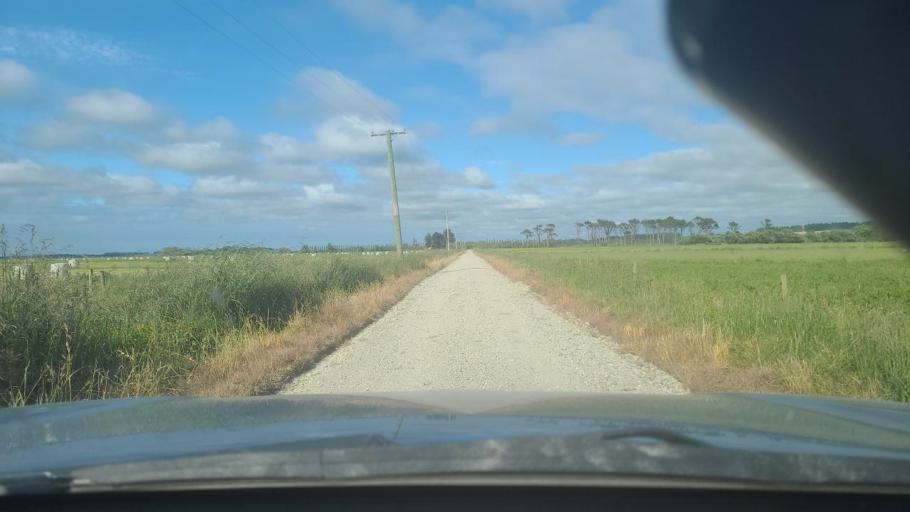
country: NZ
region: Southland
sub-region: Gore District
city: Gore
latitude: -46.4585
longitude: 168.7613
